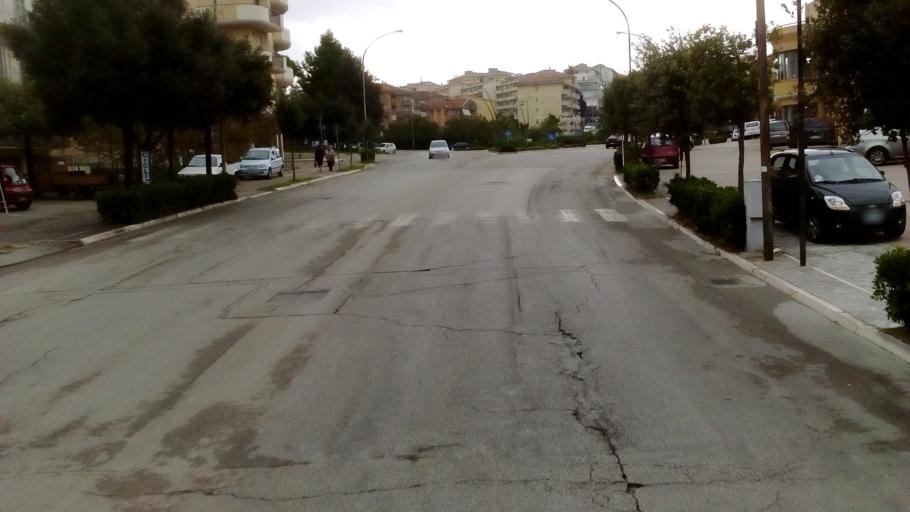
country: IT
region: Abruzzo
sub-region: Provincia di Chieti
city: Vasto
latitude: 42.1087
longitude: 14.7022
